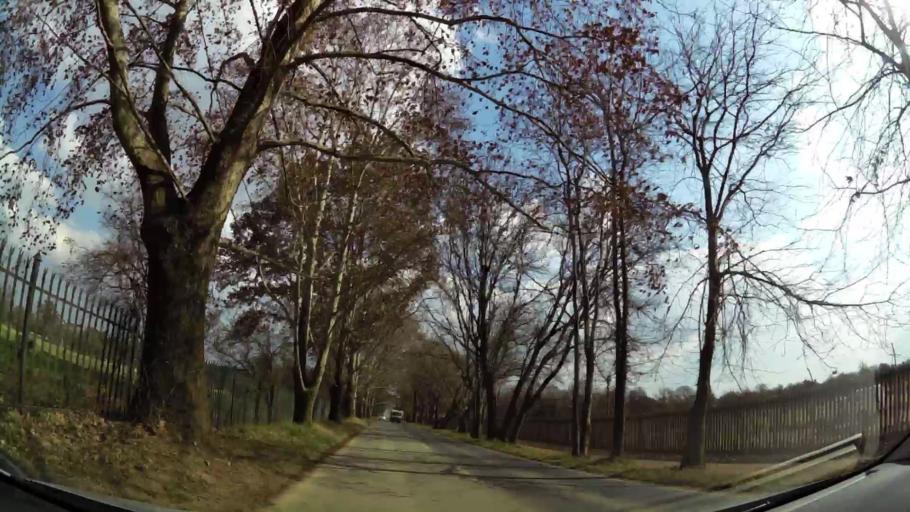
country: ZA
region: Gauteng
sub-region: City of Tshwane Metropolitan Municipality
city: Centurion
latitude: -25.8778
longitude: 28.2098
